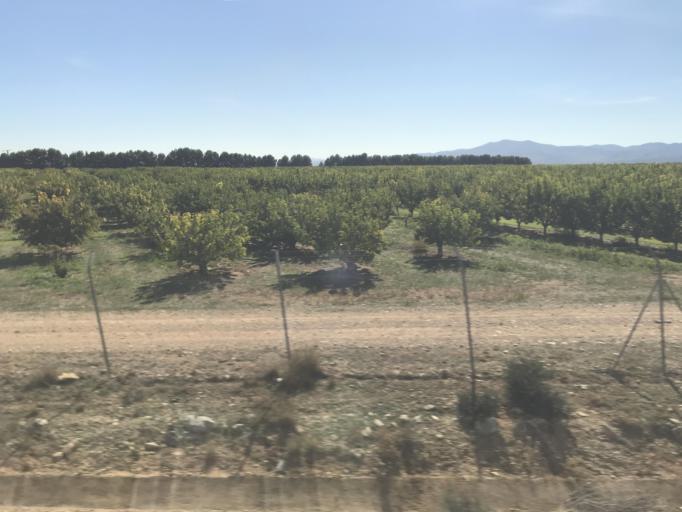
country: ES
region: Aragon
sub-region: Provincia de Zaragoza
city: Calatorao
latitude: 41.5343
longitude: -1.3750
